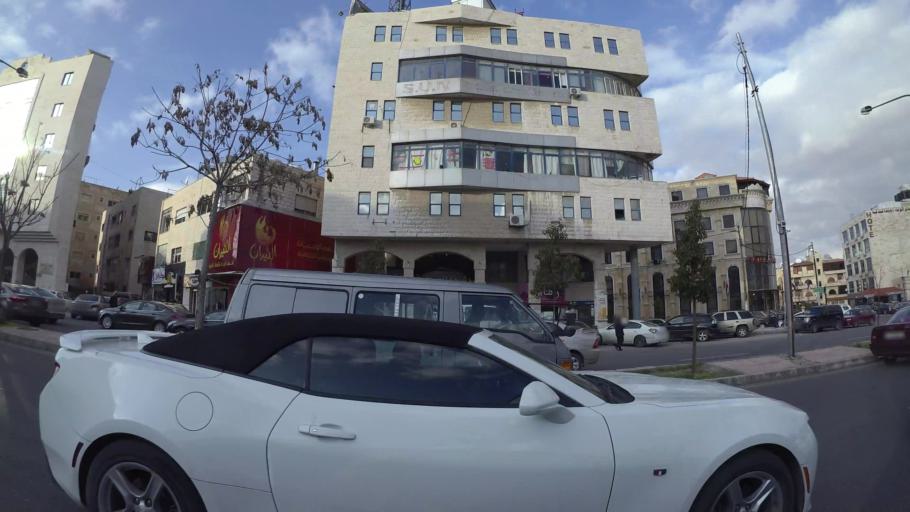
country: JO
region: Amman
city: Al Jubayhah
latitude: 31.9834
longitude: 35.8914
